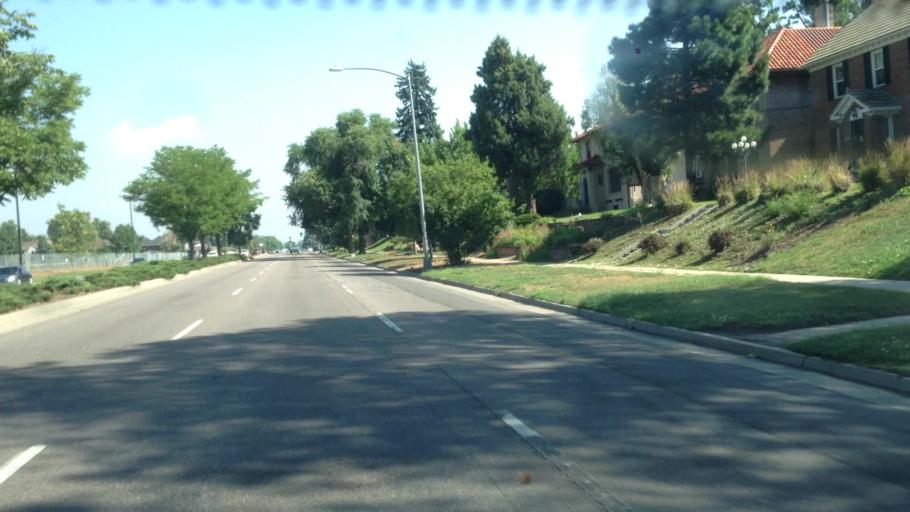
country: US
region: Colorado
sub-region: Denver County
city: Denver
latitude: 39.7520
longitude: -104.9406
